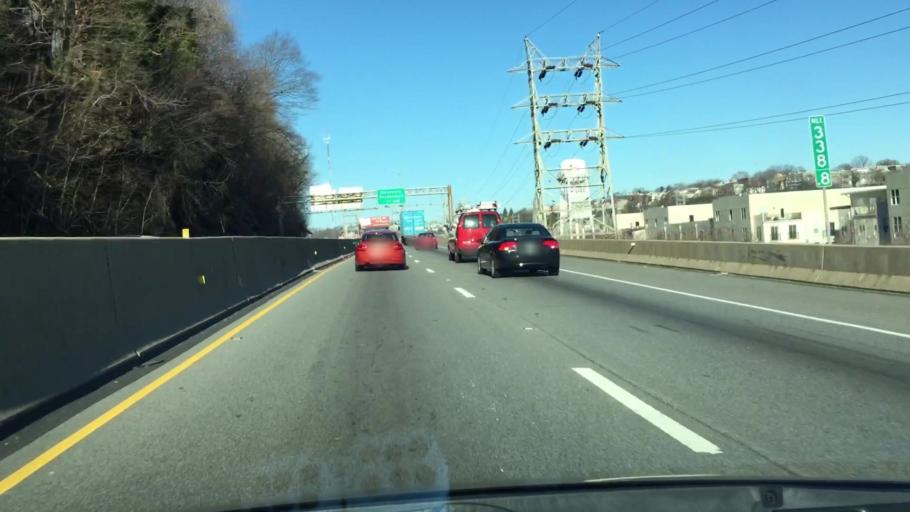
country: US
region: Pennsylvania
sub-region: Montgomery County
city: Bala-Cynwyd
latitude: 40.0174
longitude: -75.2169
